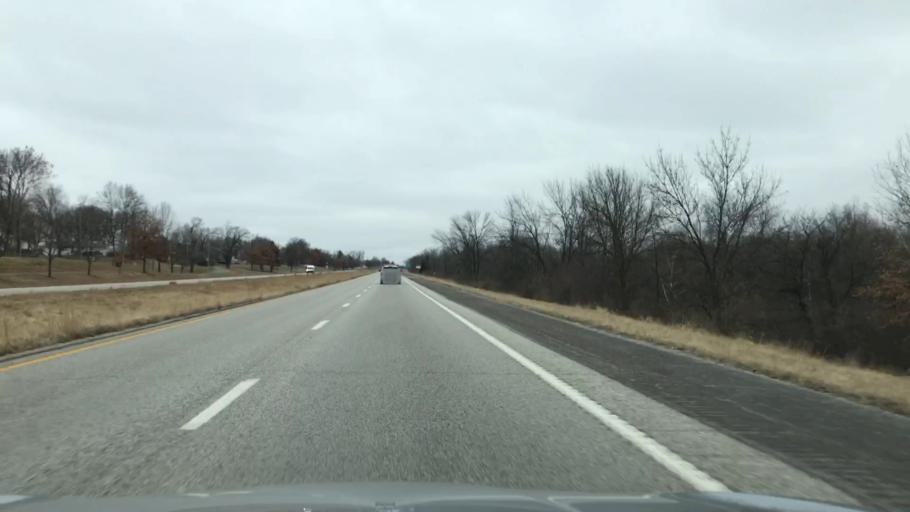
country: US
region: Missouri
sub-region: Clay County
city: Liberty
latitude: 39.2182
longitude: -94.4112
